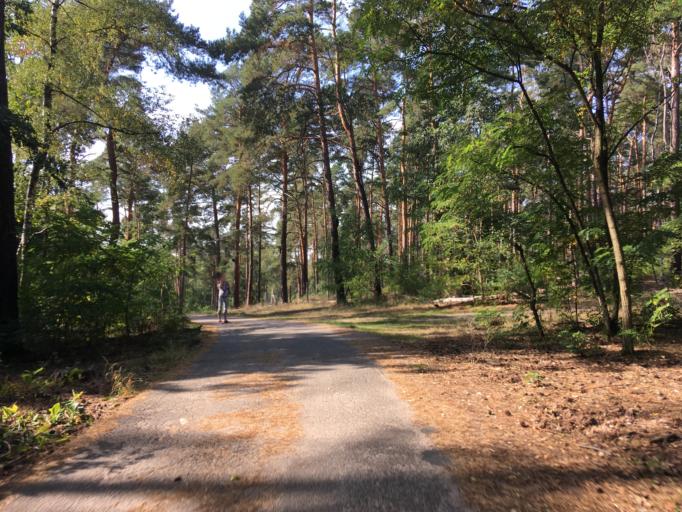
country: DE
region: Berlin
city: Muggelheim
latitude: 52.4098
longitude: 13.6449
